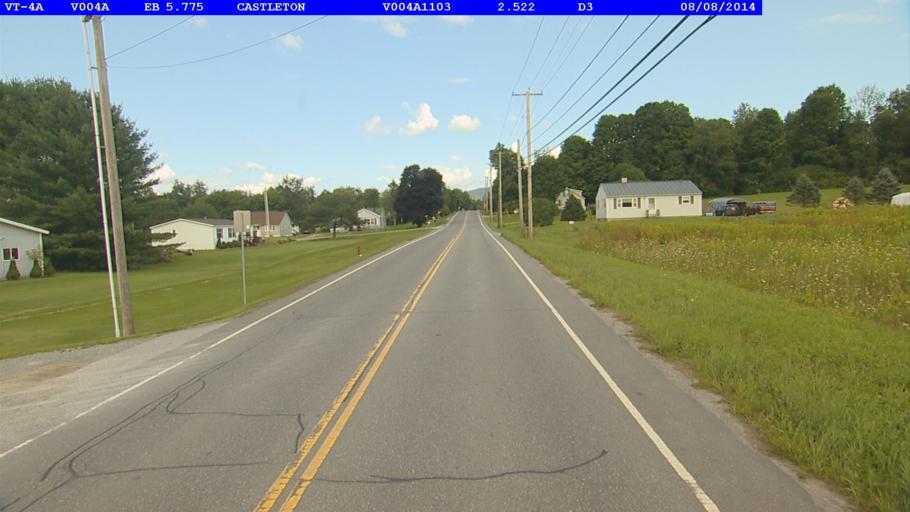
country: US
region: Vermont
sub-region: Rutland County
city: Castleton
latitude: 43.6077
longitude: -73.1939
